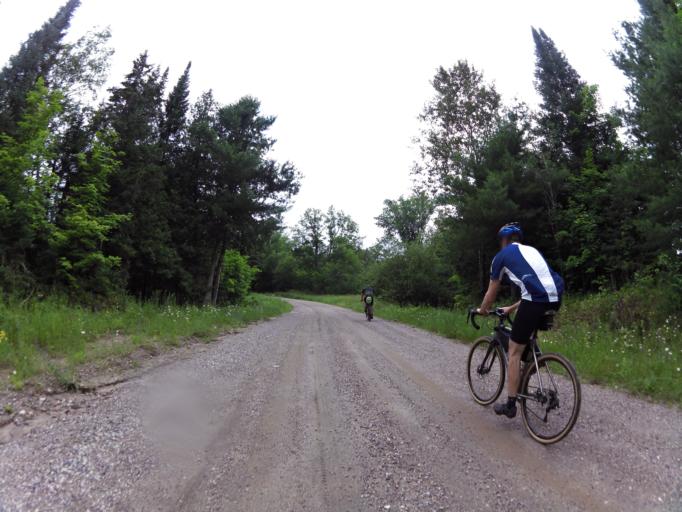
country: CA
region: Ontario
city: Renfrew
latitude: 45.0646
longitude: -76.7563
